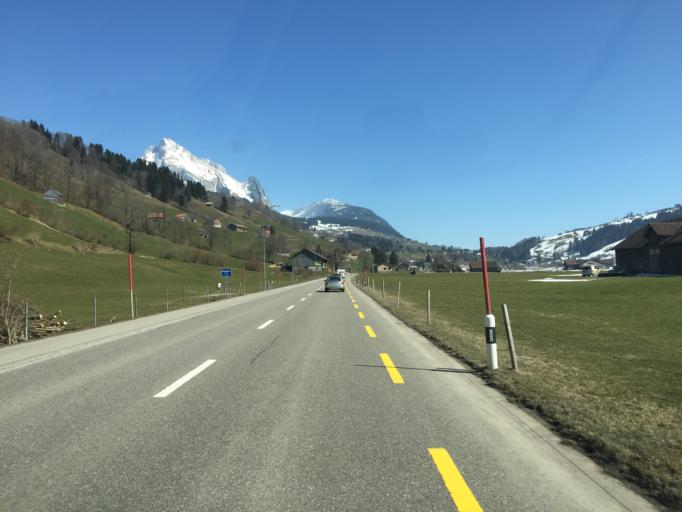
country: CH
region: Saint Gallen
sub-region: Wahlkreis Toggenburg
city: Wildhaus
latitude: 47.1949
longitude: 9.2883
